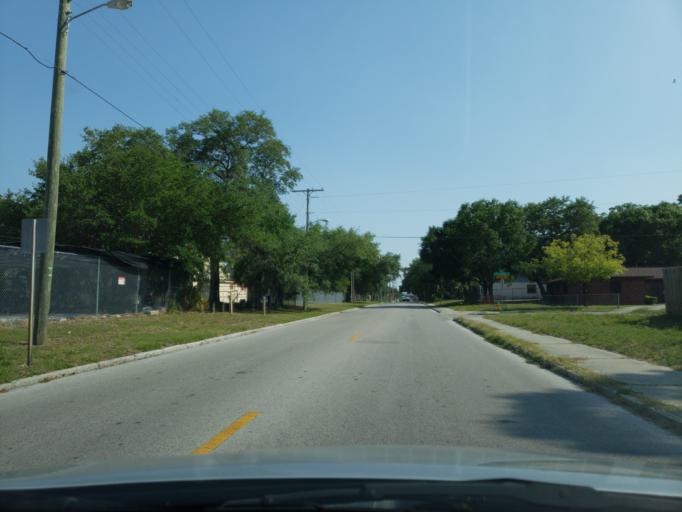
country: US
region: Florida
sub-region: Hillsborough County
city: Tampa
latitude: 27.9626
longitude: -82.4766
